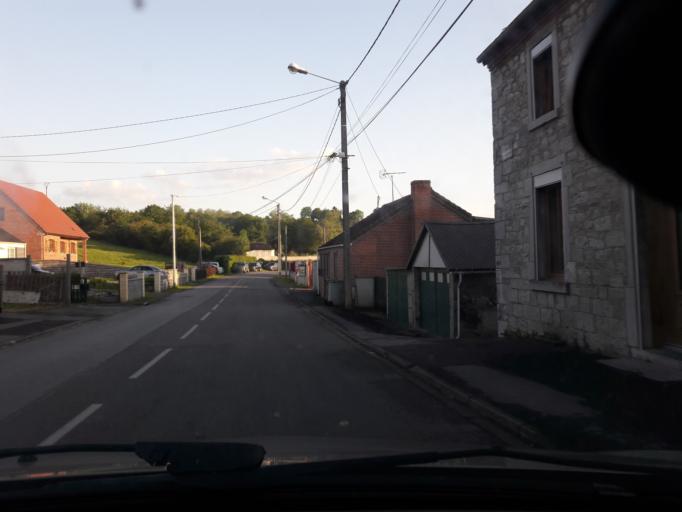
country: FR
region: Nord-Pas-de-Calais
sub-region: Departement du Nord
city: Marpent
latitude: 50.2851
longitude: 4.0717
